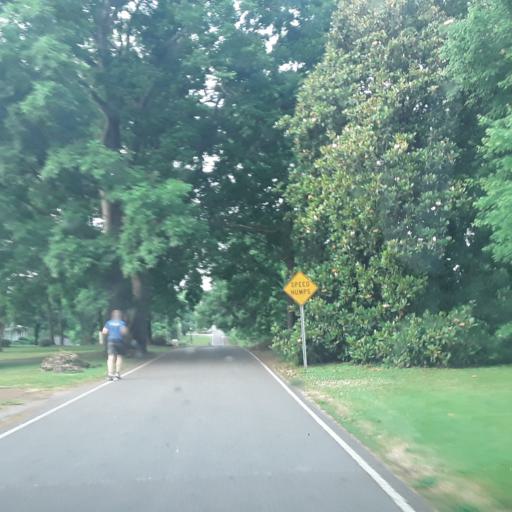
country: US
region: Tennessee
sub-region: Williamson County
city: Brentwood
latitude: 36.0594
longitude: -86.7626
